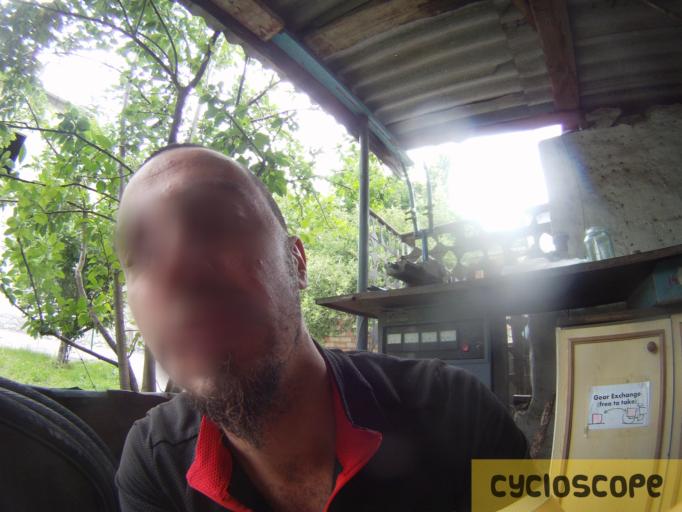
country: KG
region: Chuy
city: Bishkek
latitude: 42.8596
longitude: 74.5958
